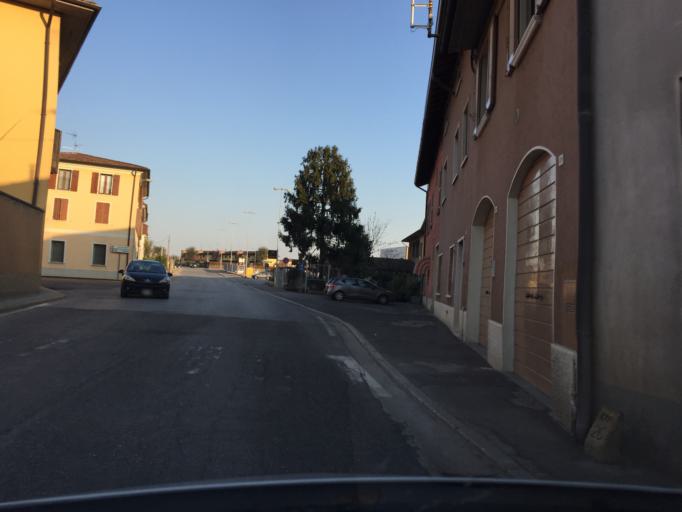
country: IT
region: Lombardy
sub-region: Provincia di Brescia
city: Pralboino
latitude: 45.2650
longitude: 10.2167
